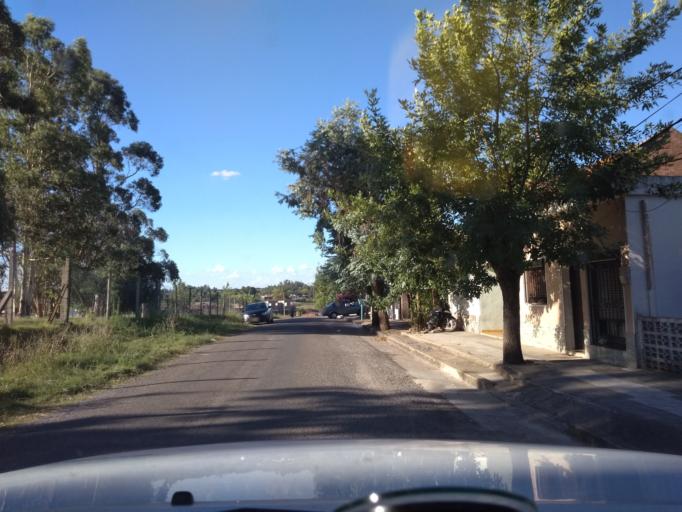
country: UY
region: Florida
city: Florida
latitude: -34.0980
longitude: -56.2272
